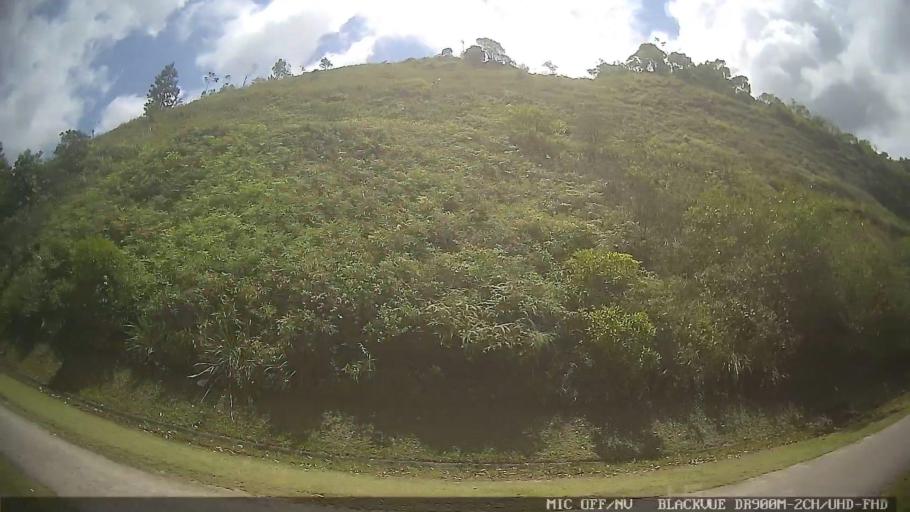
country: BR
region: Sao Paulo
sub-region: Caraguatatuba
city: Caraguatatuba
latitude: -23.6148
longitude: -45.3851
